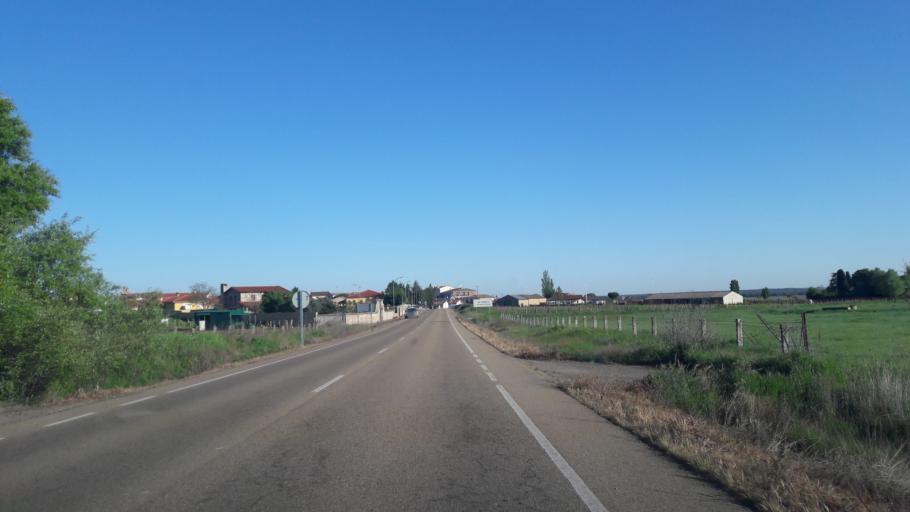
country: ES
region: Castille and Leon
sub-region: Provincia de Salamanca
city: La Fuente de San Esteban
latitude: 40.7998
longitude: -6.2528
